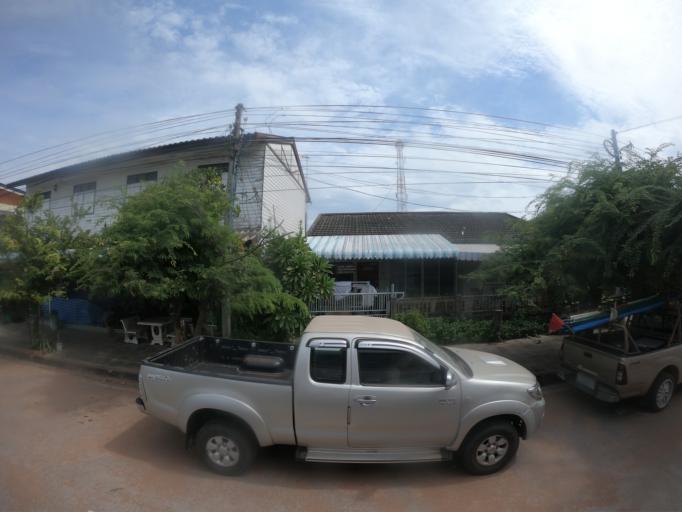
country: TH
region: Maha Sarakham
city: Chiang Yuen
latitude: 16.4077
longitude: 103.0981
